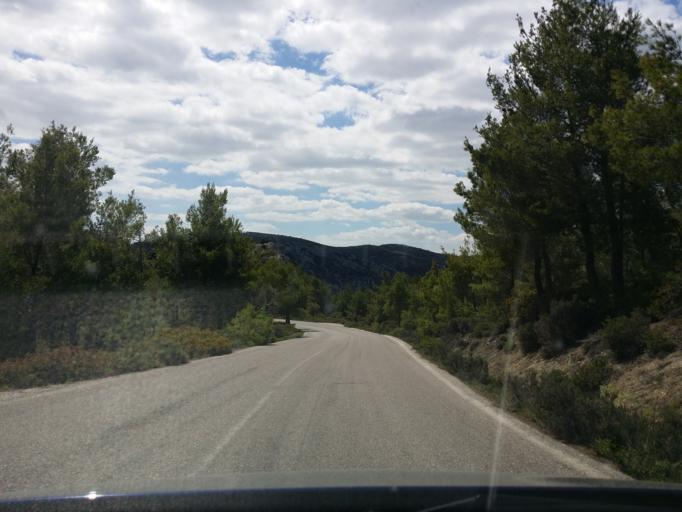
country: GR
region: Attica
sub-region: Nomarchia Dytikis Attikis
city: Fyli
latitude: 38.1279
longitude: 23.6471
